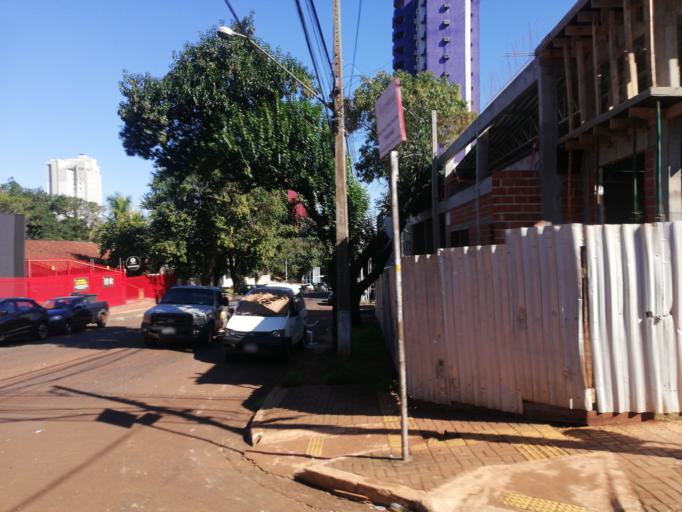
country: BR
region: Parana
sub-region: Foz Do Iguacu
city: Foz do Iguacu
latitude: -25.5411
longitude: -54.5762
